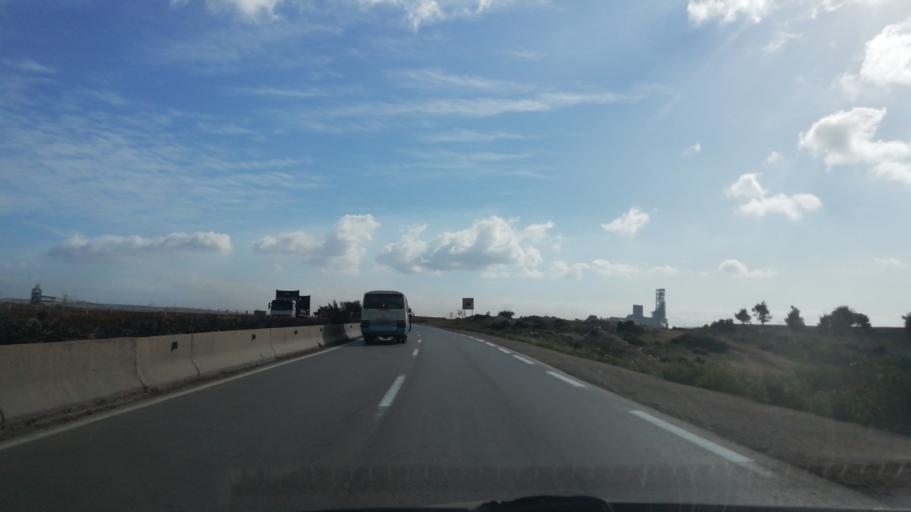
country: DZ
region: Oran
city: Ain el Bya
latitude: 35.7811
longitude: -0.2799
